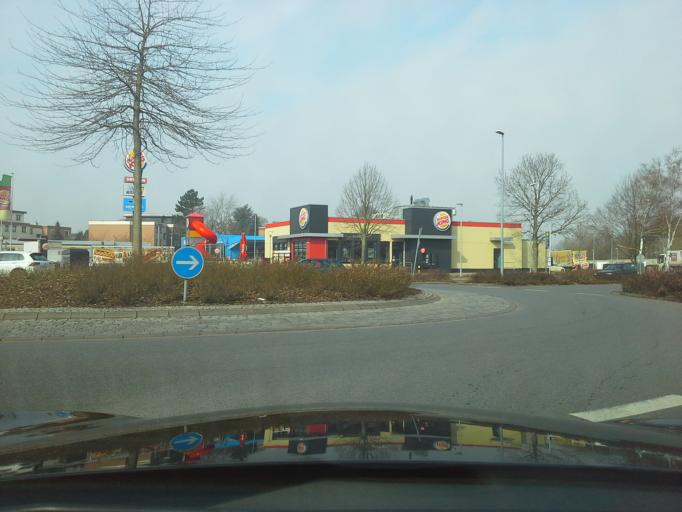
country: DE
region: Lower Saxony
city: Wunstorf
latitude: 52.4164
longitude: 9.4489
